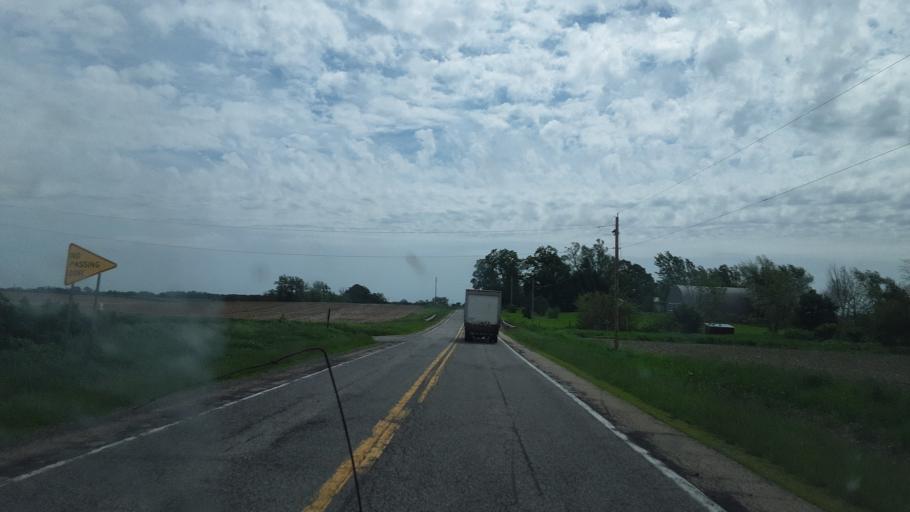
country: US
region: Illinois
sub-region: Tazewell County
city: Richmond
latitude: 40.3097
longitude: -89.3641
